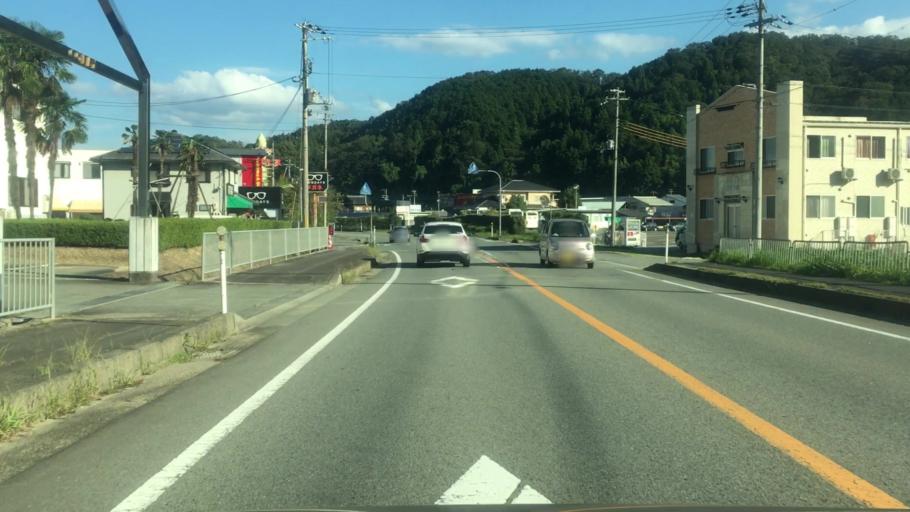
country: JP
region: Hyogo
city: Toyooka
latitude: 35.5554
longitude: 134.8335
